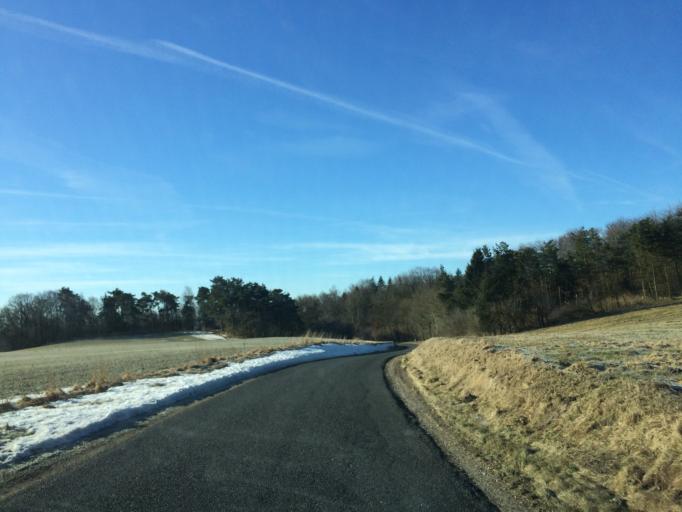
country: DK
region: North Denmark
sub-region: Mariagerfjord Kommune
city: Hobro
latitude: 56.6177
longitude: 9.6450
